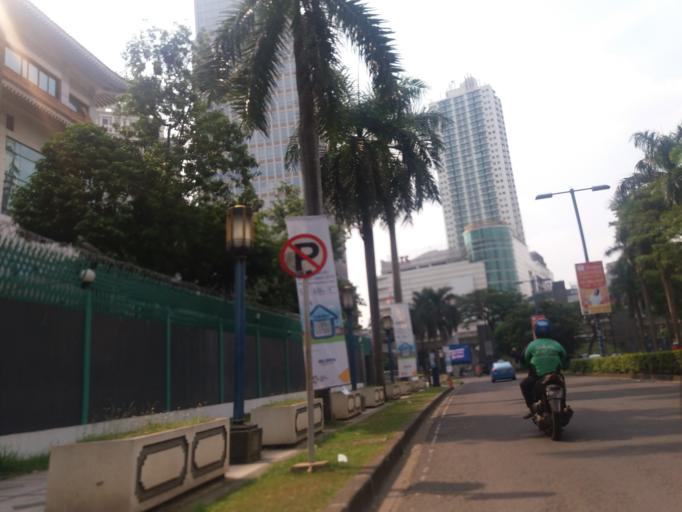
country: ID
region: Jakarta Raya
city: Jakarta
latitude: -6.2259
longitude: 106.8258
